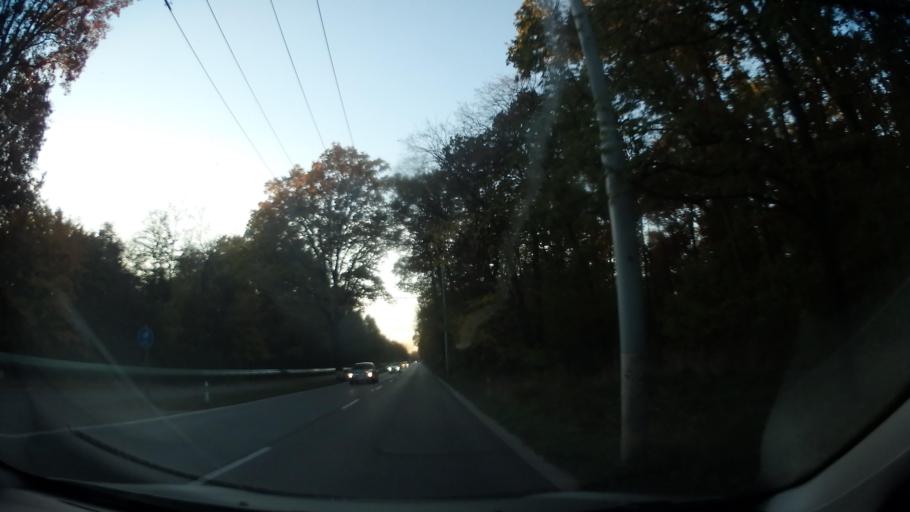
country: CZ
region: Pardubicky
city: Rybitvi
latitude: 50.0684
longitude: 15.6992
